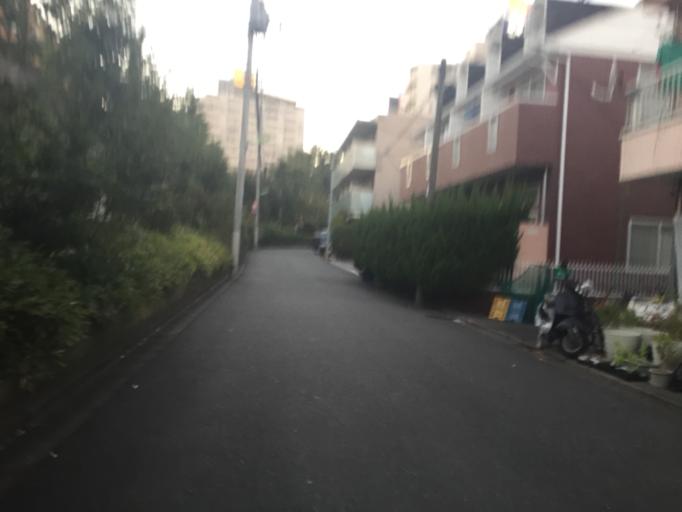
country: JP
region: Tokyo
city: Tokyo
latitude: 35.6304
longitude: 139.6579
